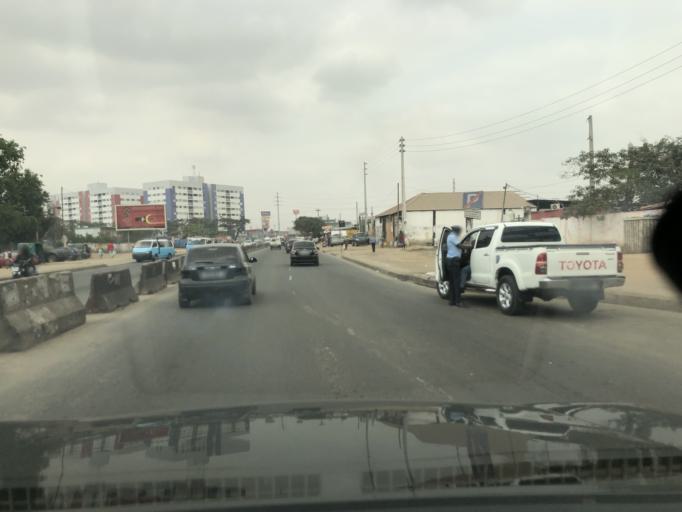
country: AO
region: Luanda
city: Luanda
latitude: -8.8454
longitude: 13.2845
